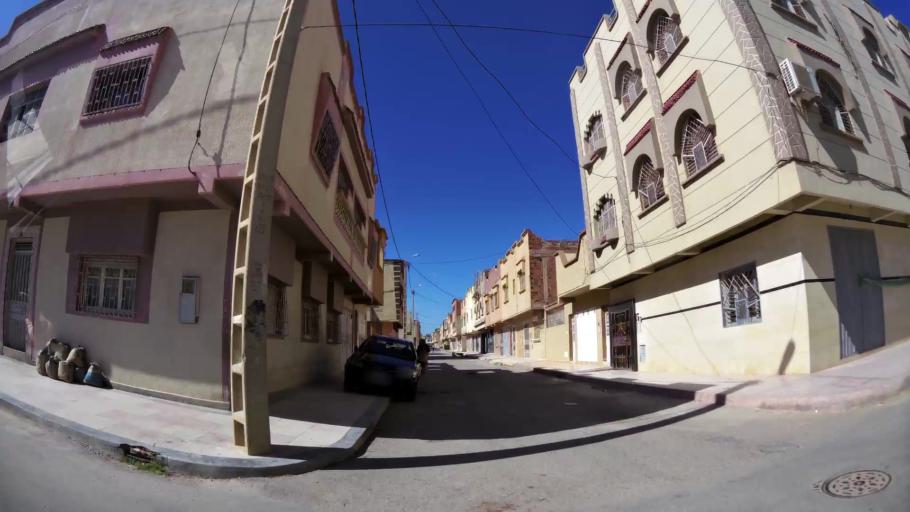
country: MA
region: Oriental
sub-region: Oujda-Angad
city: Oujda
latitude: 34.6553
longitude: -1.9342
